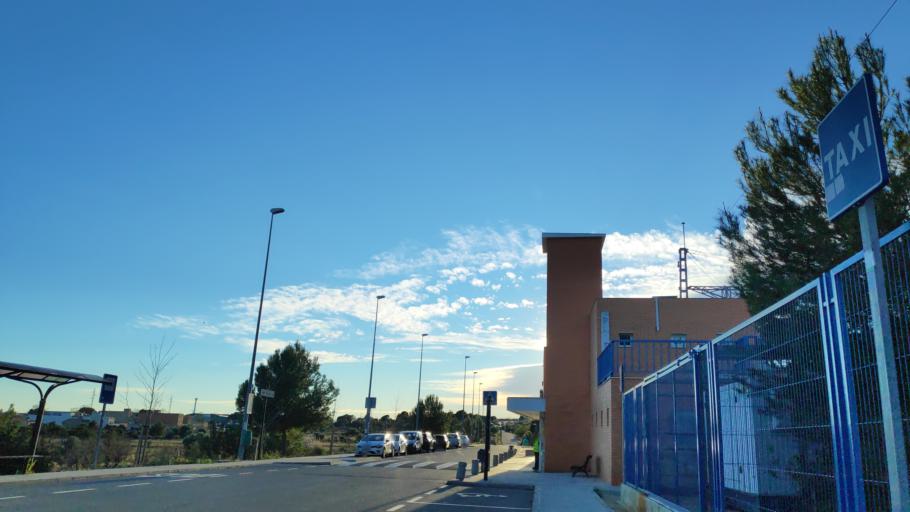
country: ES
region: Valencia
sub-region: Provincia de Castello
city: Benicassim
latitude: 40.0583
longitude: 0.0583
